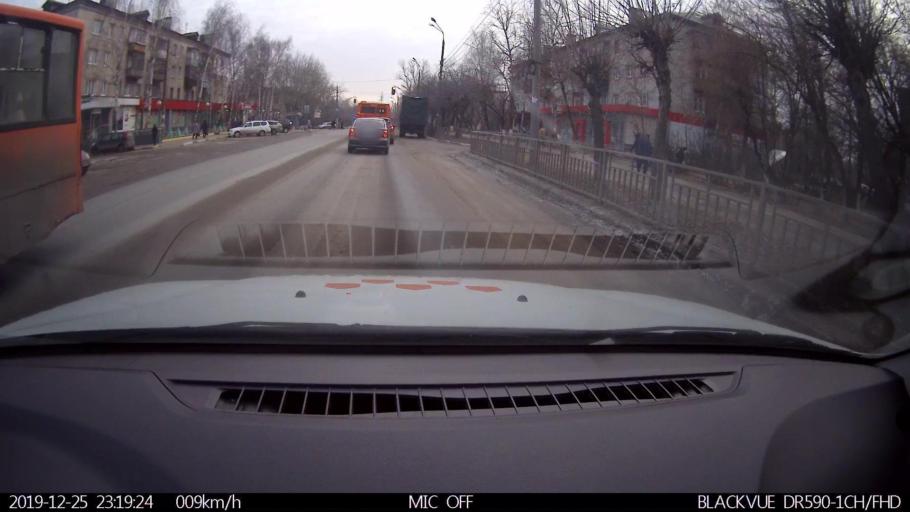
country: RU
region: Nizjnij Novgorod
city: Gorbatovka
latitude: 56.3544
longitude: 43.8315
